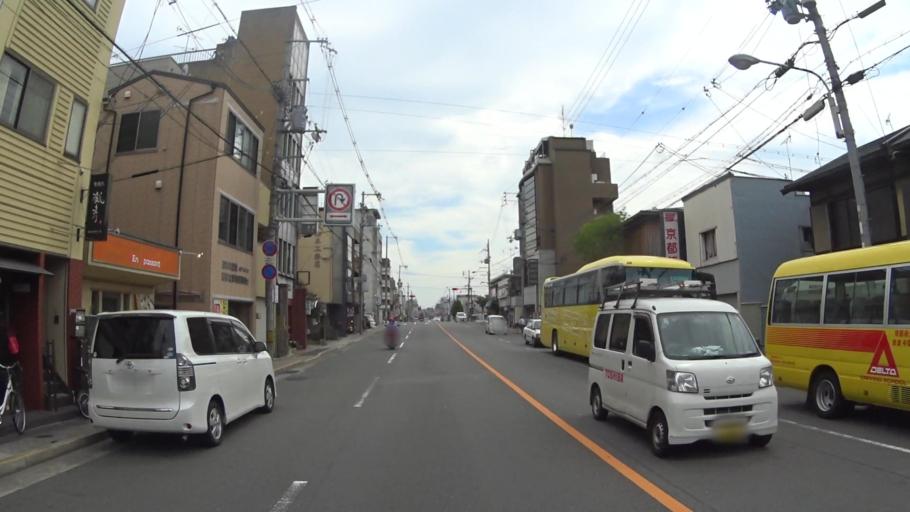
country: JP
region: Kyoto
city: Kyoto
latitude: 35.0165
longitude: 135.7785
